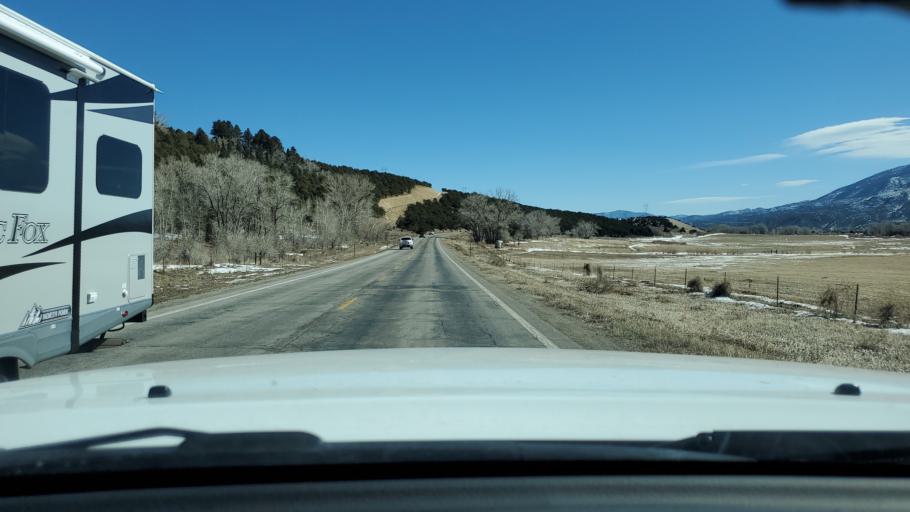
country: US
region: Colorado
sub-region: Chaffee County
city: Salida
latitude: 38.5367
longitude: -106.1558
